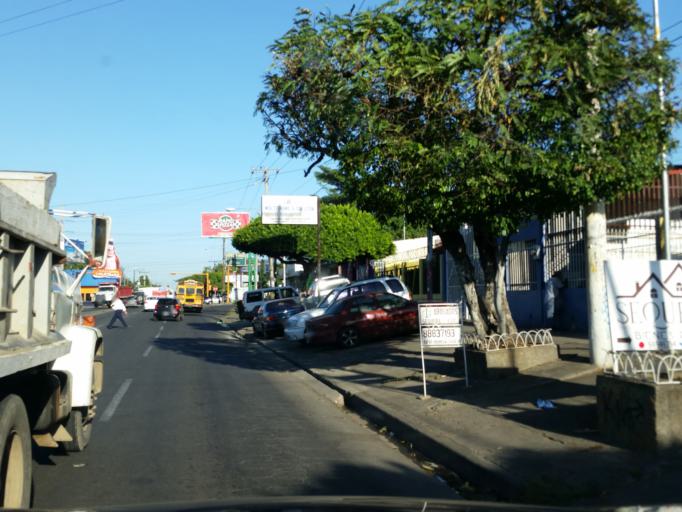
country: NI
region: Managua
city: Ciudad Sandino
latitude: 12.1525
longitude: -86.3056
